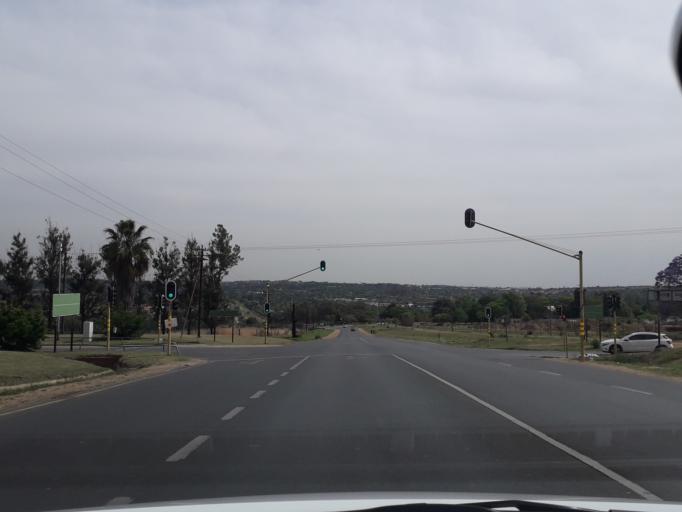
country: ZA
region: Gauteng
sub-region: City of Johannesburg Metropolitan Municipality
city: Diepsloot
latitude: -26.0006
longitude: 28.0431
